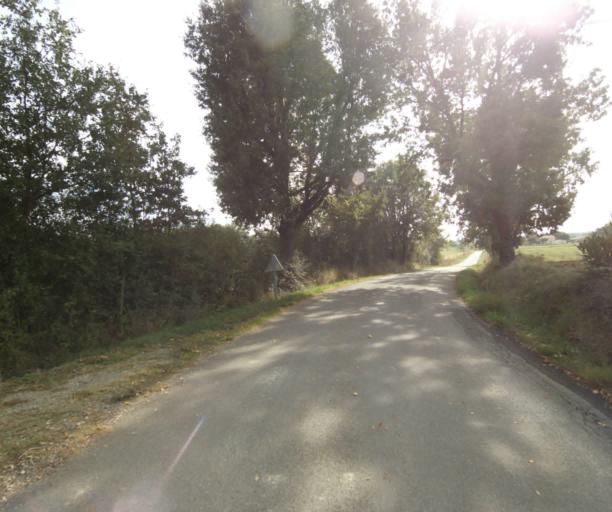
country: FR
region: Midi-Pyrenees
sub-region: Departement du Tarn-et-Garonne
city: Labastide-Saint-Pierre
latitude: 43.9072
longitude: 1.3853
